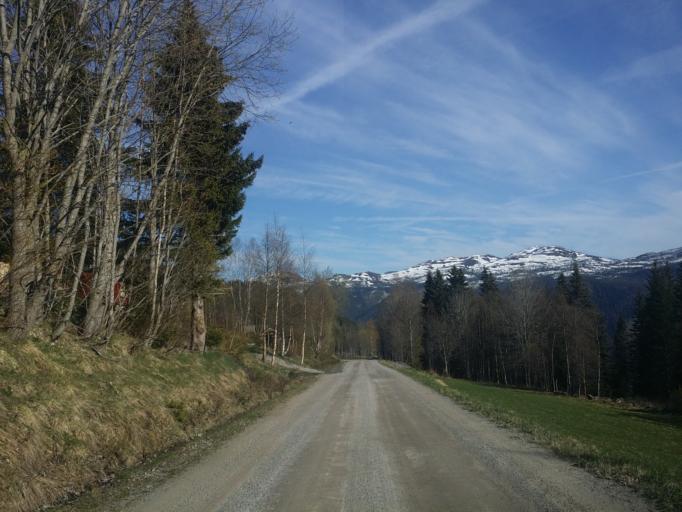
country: NO
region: Telemark
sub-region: Seljord
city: Seljord
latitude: 59.6219
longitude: 8.6879
